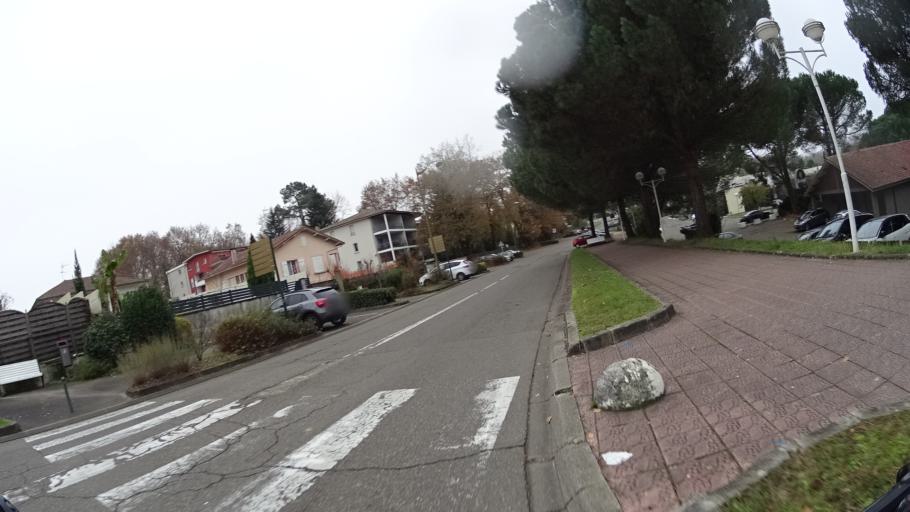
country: FR
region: Aquitaine
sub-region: Departement des Landes
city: Saint-Paul-les-Dax
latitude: 43.7273
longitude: -1.0632
